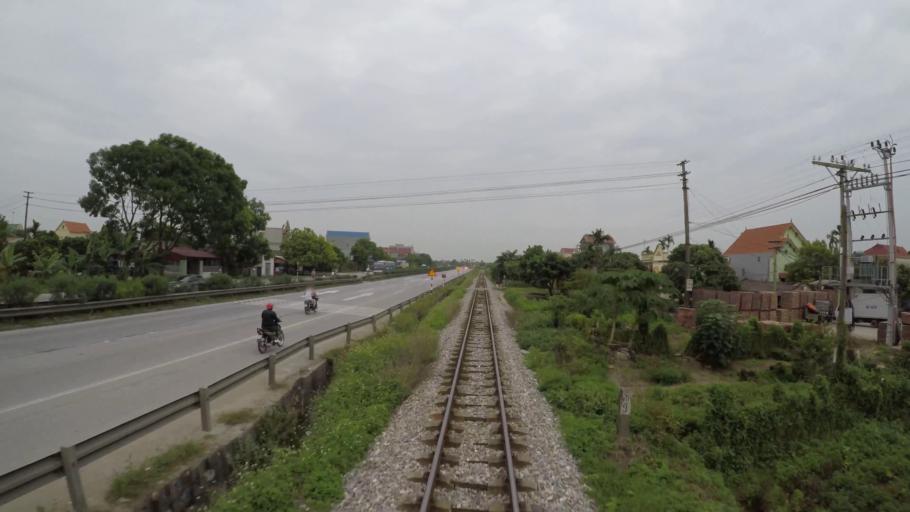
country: VN
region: Hai Duong
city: Phu Thai
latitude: 20.9762
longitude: 106.4325
